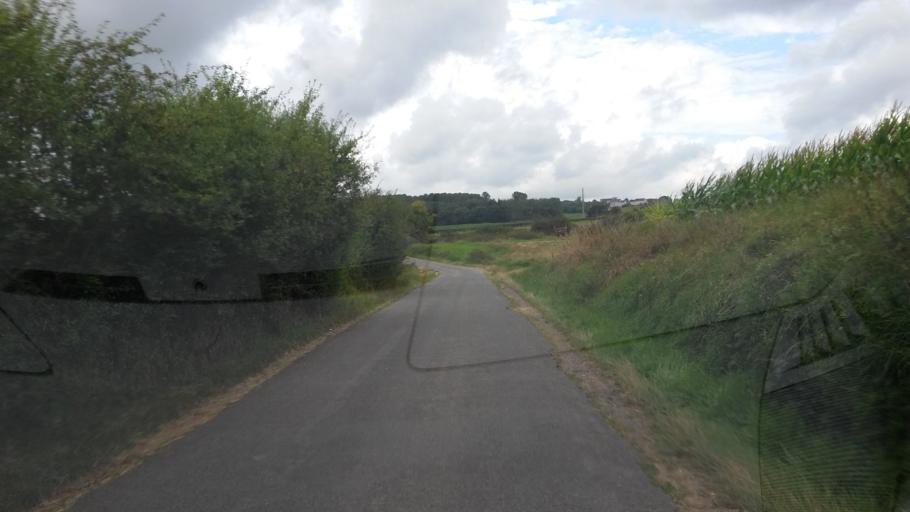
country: LU
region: Luxembourg
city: Eischen
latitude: 49.6686
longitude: 5.8538
